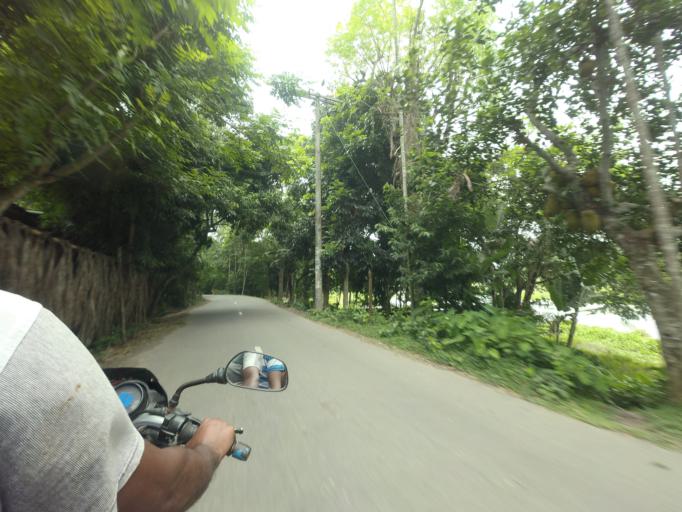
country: BD
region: Khulna
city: Kalia
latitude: 23.1761
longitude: 89.6469
